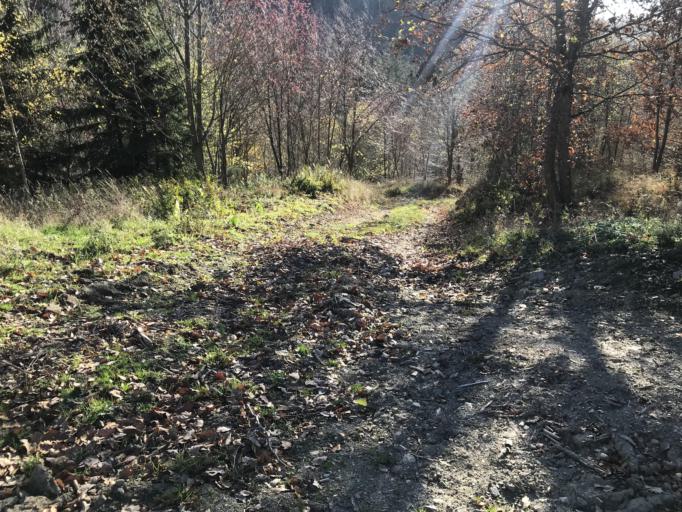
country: DE
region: Saxony-Anhalt
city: Huttenrode
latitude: 51.7516
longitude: 10.8938
